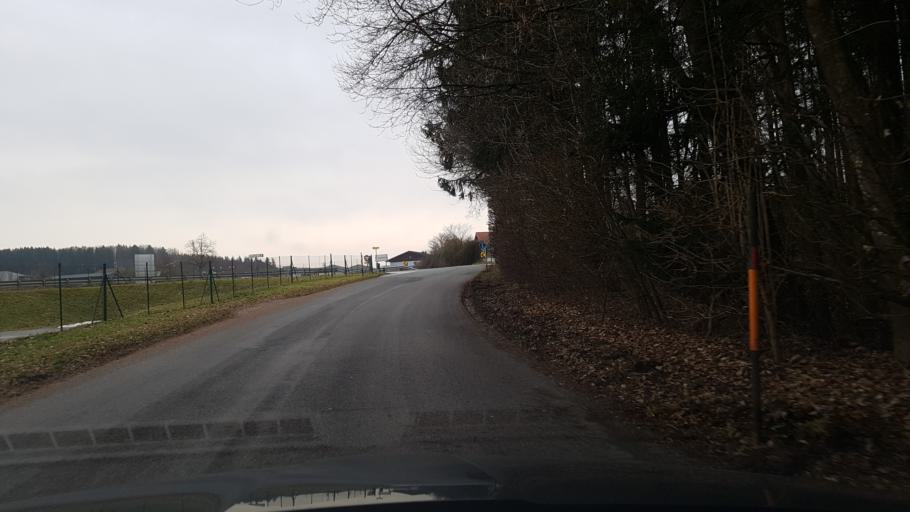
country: AT
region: Salzburg
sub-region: Politischer Bezirk Salzburg-Umgebung
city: Lamprechtshausen
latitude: 48.0049
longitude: 12.9605
